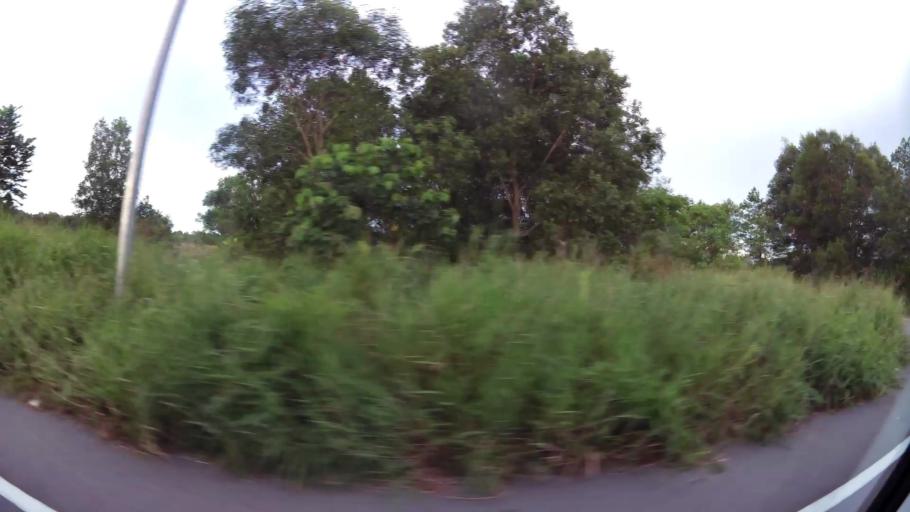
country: BN
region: Brunei and Muara
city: Bandar Seri Begawan
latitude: 4.9981
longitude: 114.9901
